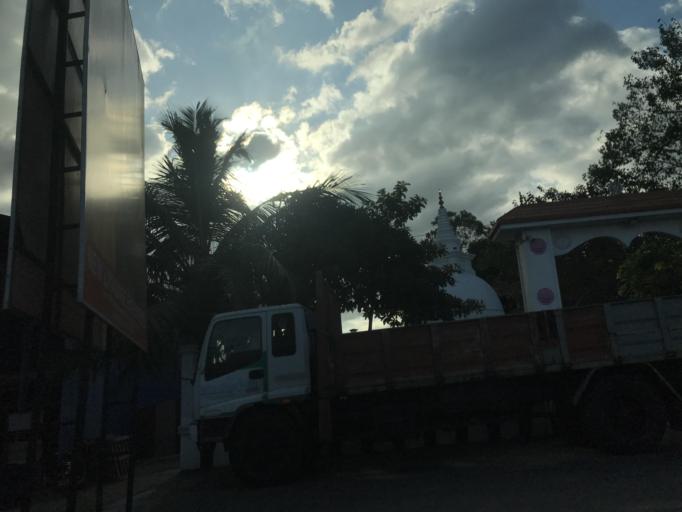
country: LK
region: Western
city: Gampaha
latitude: 7.0997
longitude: 79.9912
